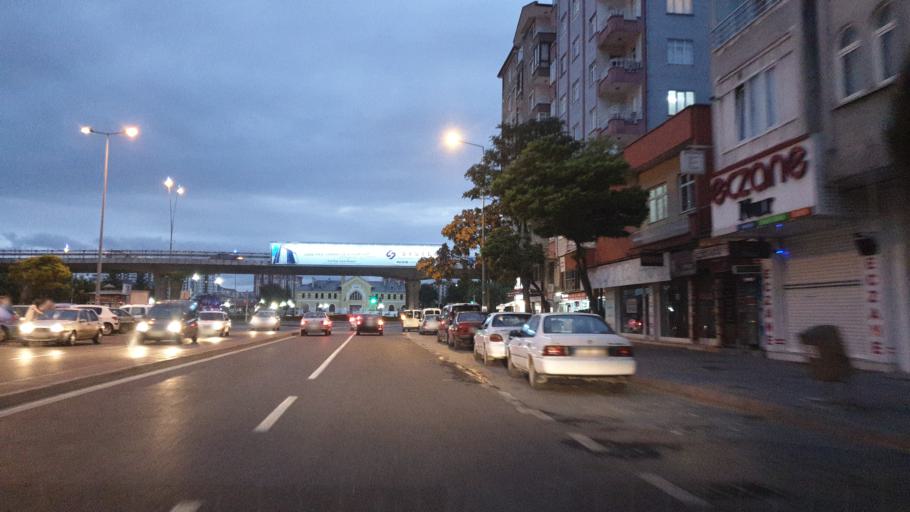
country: TR
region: Kayseri
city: Kayseri
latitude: 38.7284
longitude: 35.4790
